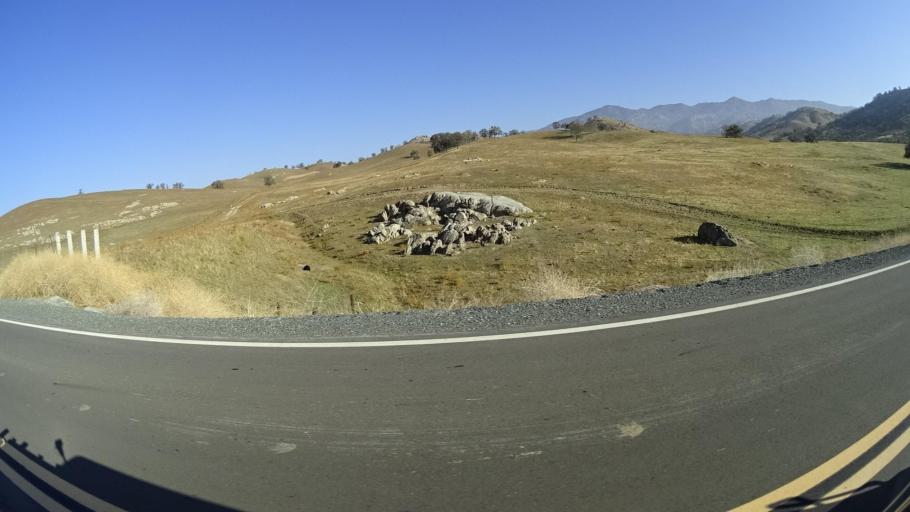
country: US
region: California
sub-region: Tulare County
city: Richgrove
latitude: 35.7107
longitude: -118.8418
